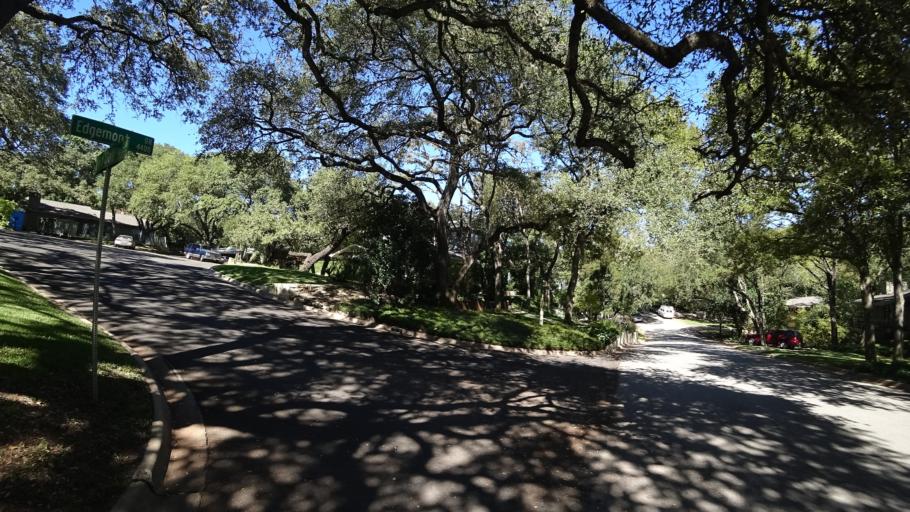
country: US
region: Texas
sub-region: Travis County
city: West Lake Hills
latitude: 30.3243
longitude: -97.7668
